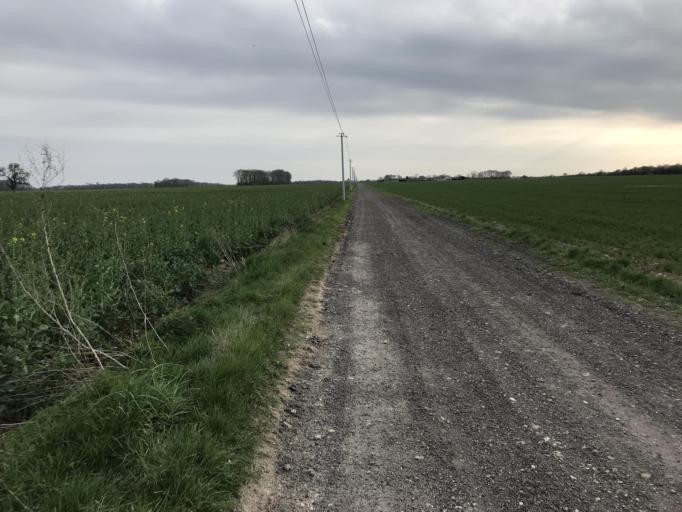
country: FR
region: Ile-de-France
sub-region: Departement de l'Essonne
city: Les Molieres
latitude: 48.6668
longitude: 2.0519
